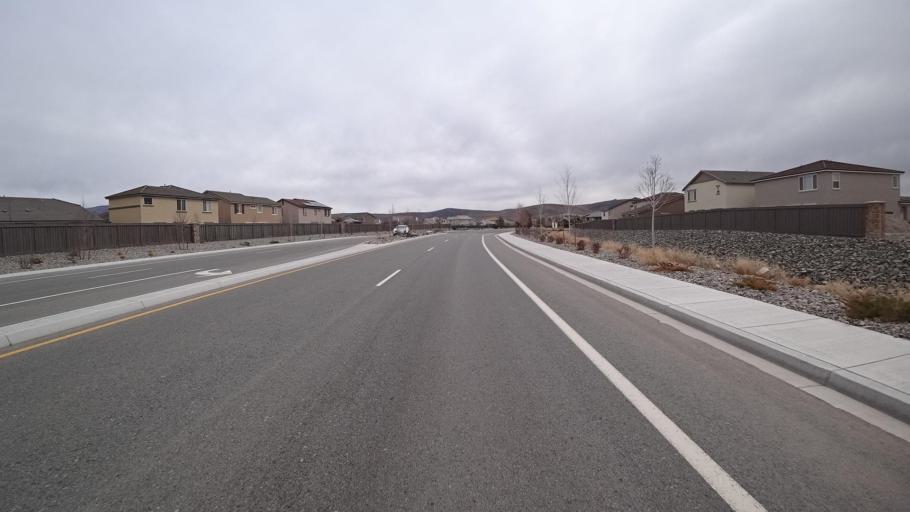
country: US
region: Nevada
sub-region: Washoe County
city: Spanish Springs
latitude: 39.6151
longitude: -119.7043
